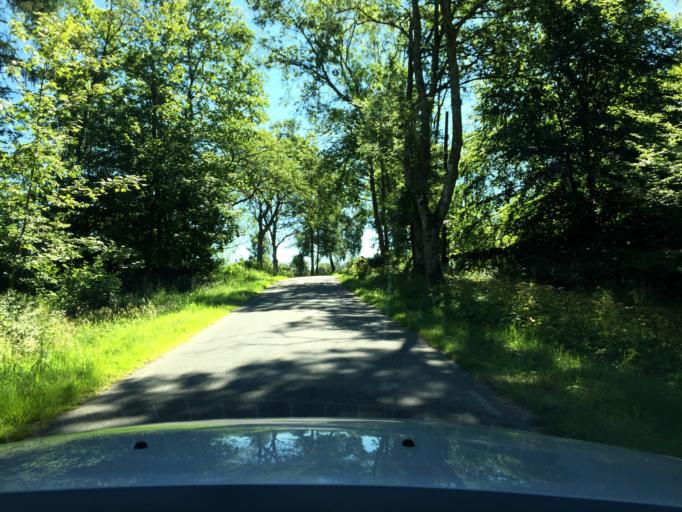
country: SE
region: Skane
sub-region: Hassleholms Kommun
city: Sosdala
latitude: 56.0190
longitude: 13.5853
